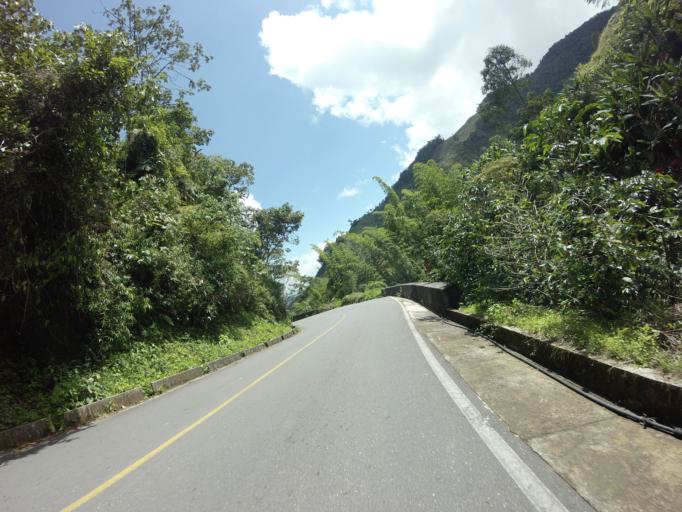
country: CO
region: Caldas
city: Marquetalia
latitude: 5.2889
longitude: -75.1064
